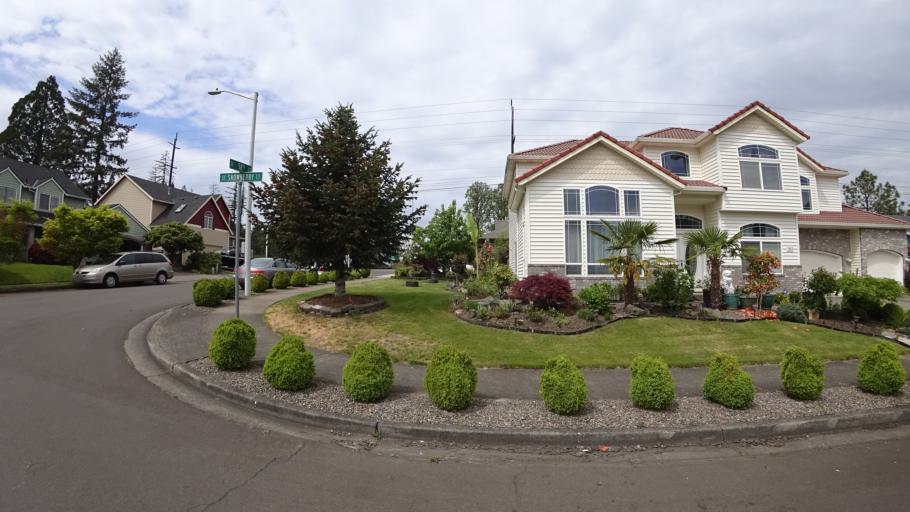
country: US
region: Oregon
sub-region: Washington County
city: Rockcreek
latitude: 45.5194
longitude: -122.9216
